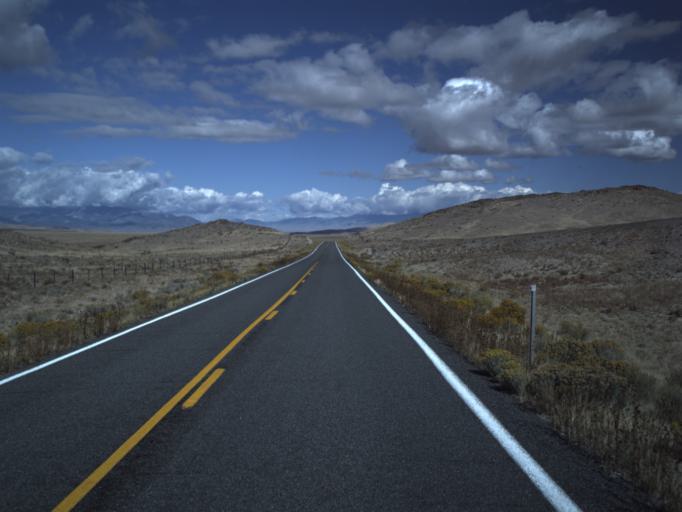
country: US
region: Utah
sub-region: Beaver County
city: Milford
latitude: 38.6231
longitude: -113.8486
